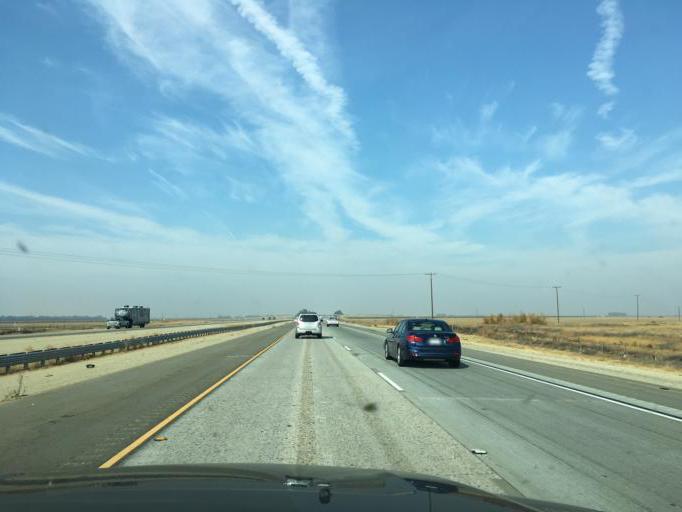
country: US
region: California
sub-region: Kern County
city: Lost Hills
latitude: 35.5667
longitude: -119.6072
